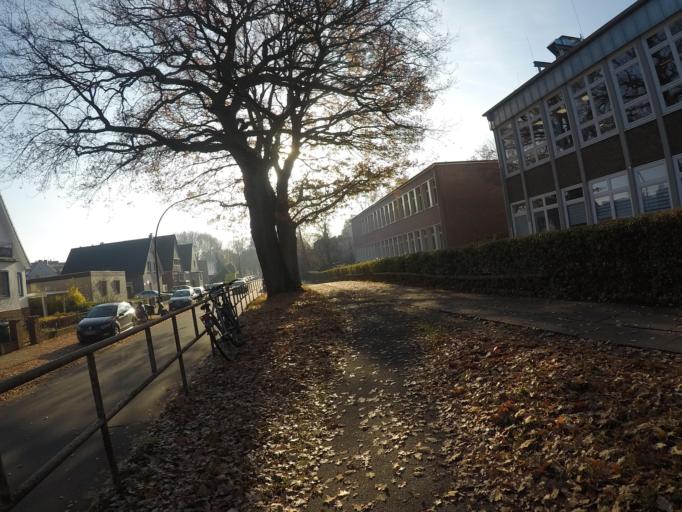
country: DE
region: Hamburg
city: Stellingen
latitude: 53.6005
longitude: 9.9256
